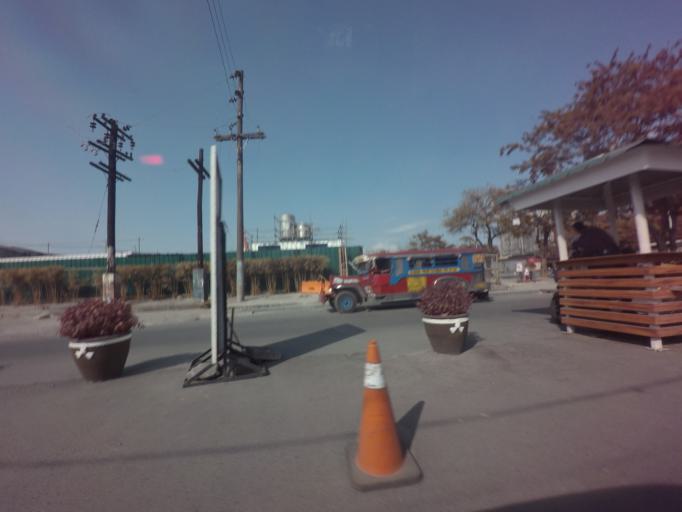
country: PH
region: Calabarzon
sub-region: Province of Rizal
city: Taguig
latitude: 14.5064
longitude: 121.0398
